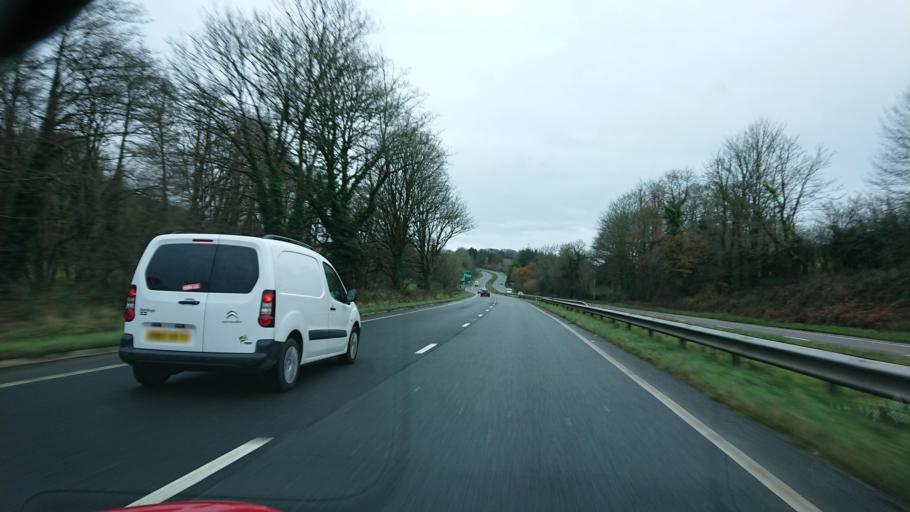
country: GB
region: England
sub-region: Cornwall
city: Liskeard
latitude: 50.4189
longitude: -4.3988
